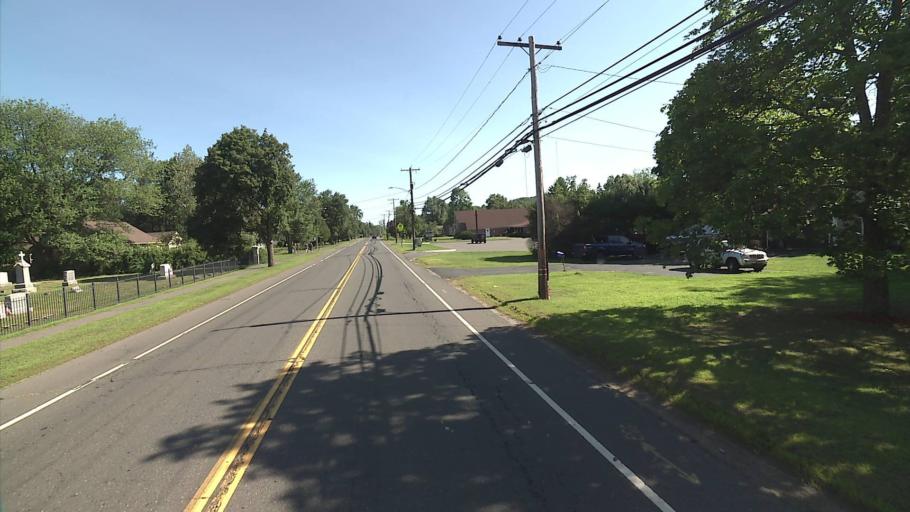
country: US
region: Connecticut
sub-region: Hartford County
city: Plainville
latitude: 41.6834
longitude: -72.8541
